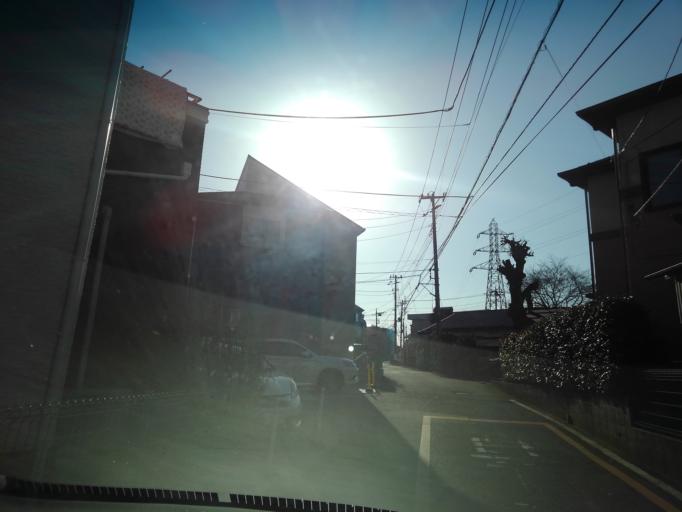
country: JP
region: Saitama
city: Tokorozawa
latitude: 35.7919
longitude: 139.4396
